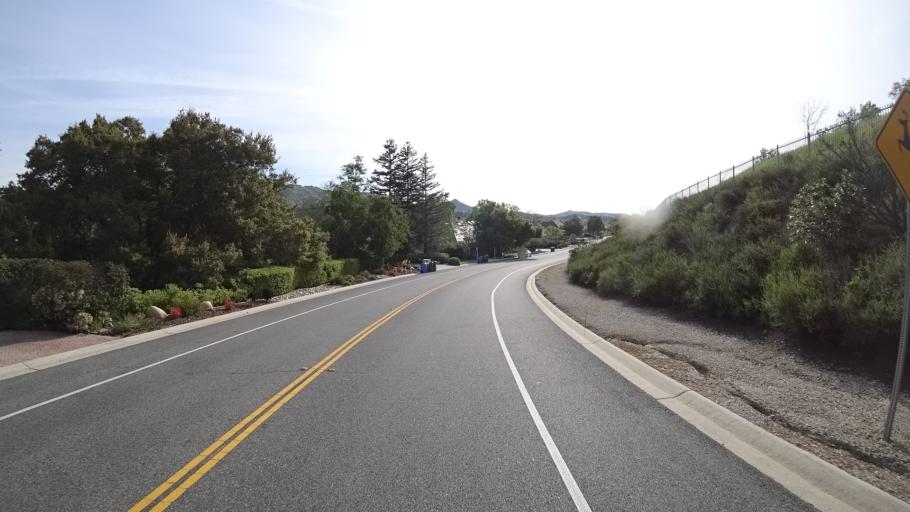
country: US
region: California
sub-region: Ventura County
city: Thousand Oaks
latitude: 34.1892
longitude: -118.8038
